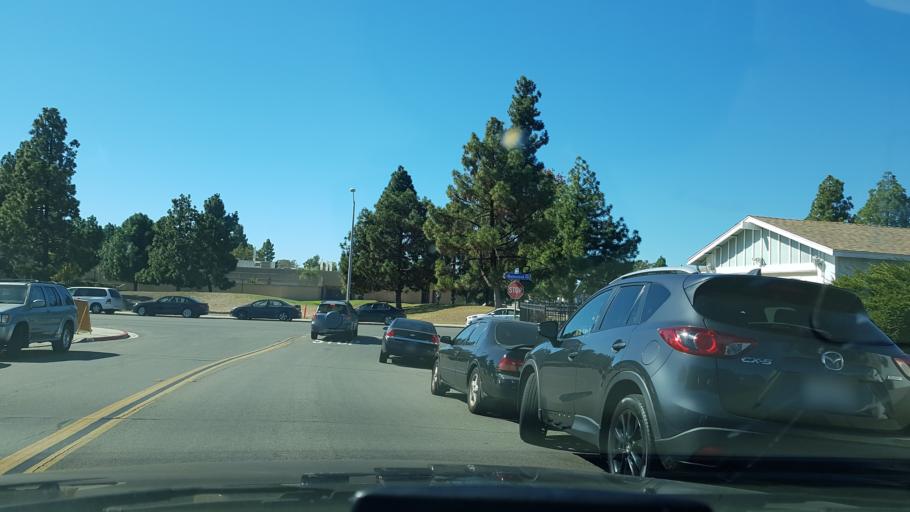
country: US
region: California
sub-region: San Diego County
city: Fairbanks Ranch
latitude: 32.9113
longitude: -117.1382
